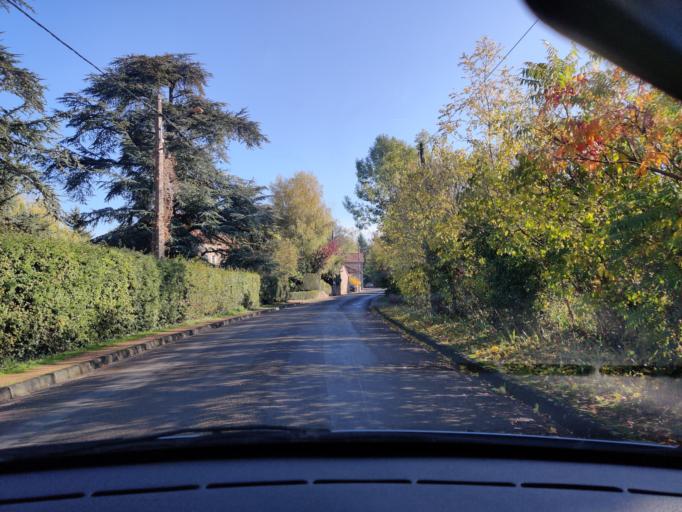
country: FR
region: Auvergne
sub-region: Departement du Puy-de-Dome
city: Aigueperse
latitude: 46.0411
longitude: 3.1309
